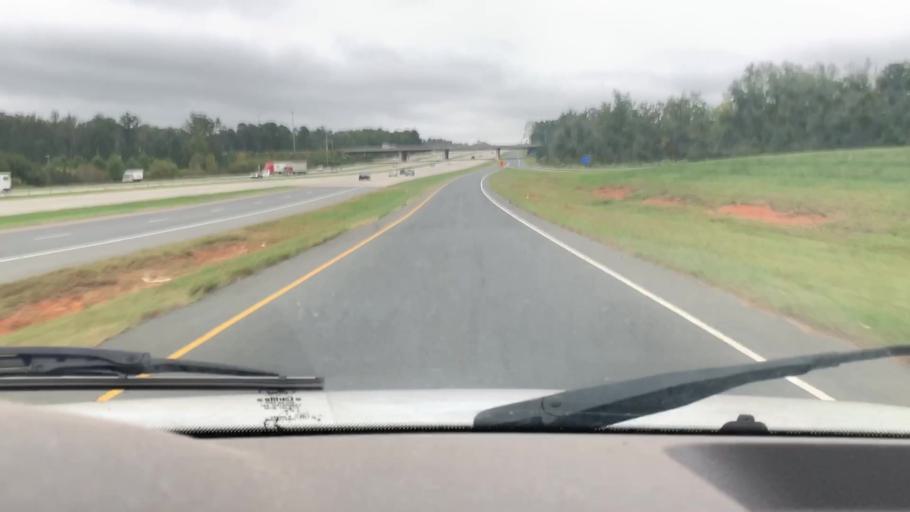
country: US
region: North Carolina
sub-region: Mecklenburg County
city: Huntersville
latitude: 35.3644
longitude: -80.8328
